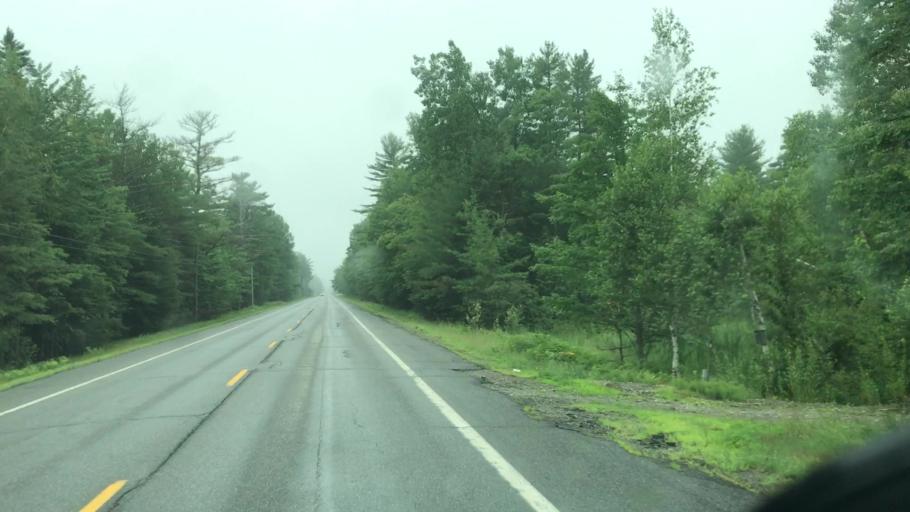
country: US
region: Maine
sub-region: Penobscot County
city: Howland
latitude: 45.2459
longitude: -68.6398
